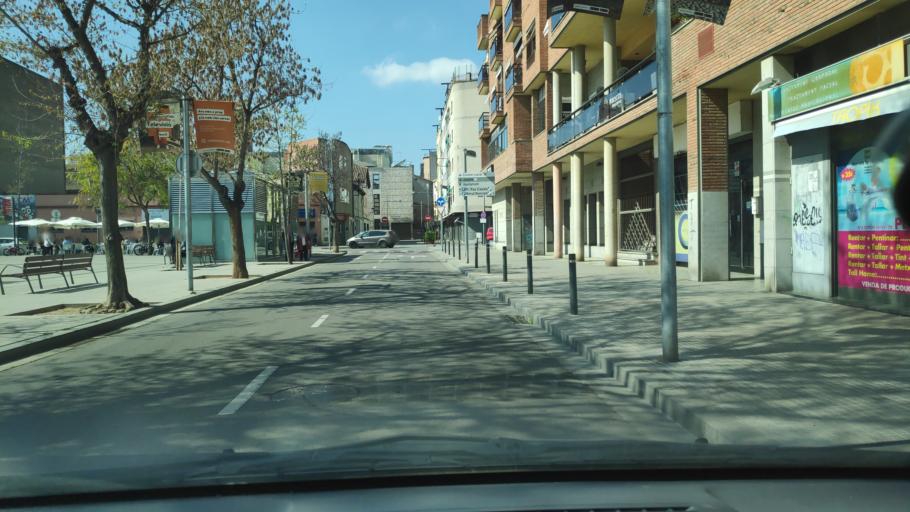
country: ES
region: Catalonia
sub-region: Provincia de Barcelona
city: Mollet del Valles
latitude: 41.5389
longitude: 2.2154
